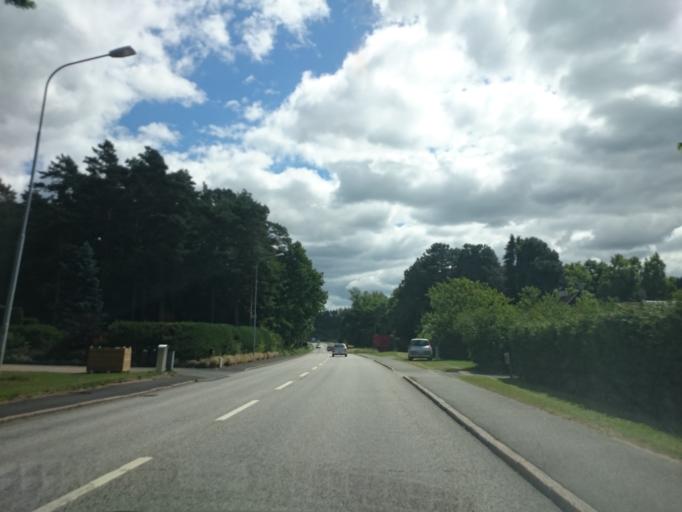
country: SE
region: Skane
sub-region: Kristianstads Kommun
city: Degeberga
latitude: 55.8283
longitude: 14.0930
